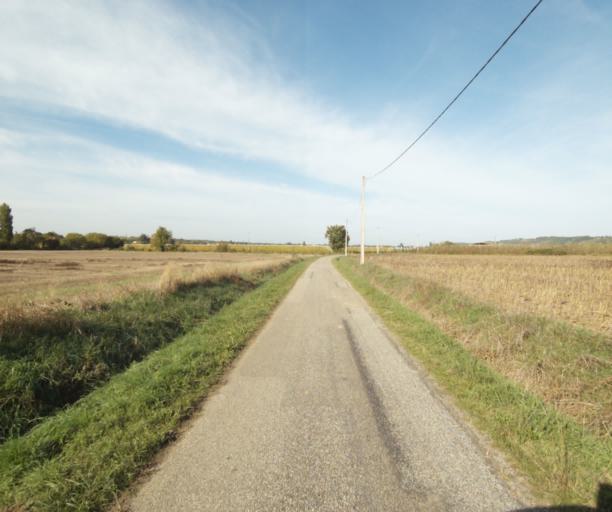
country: FR
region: Midi-Pyrenees
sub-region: Departement du Tarn-et-Garonne
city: Nohic
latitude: 43.9142
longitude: 1.4363
